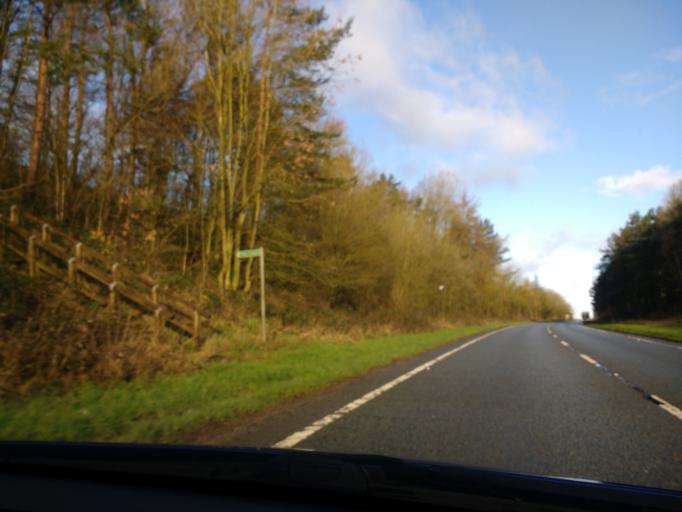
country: GB
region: England
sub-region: Cumbria
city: Cockermouth
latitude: 54.6545
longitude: -3.3757
